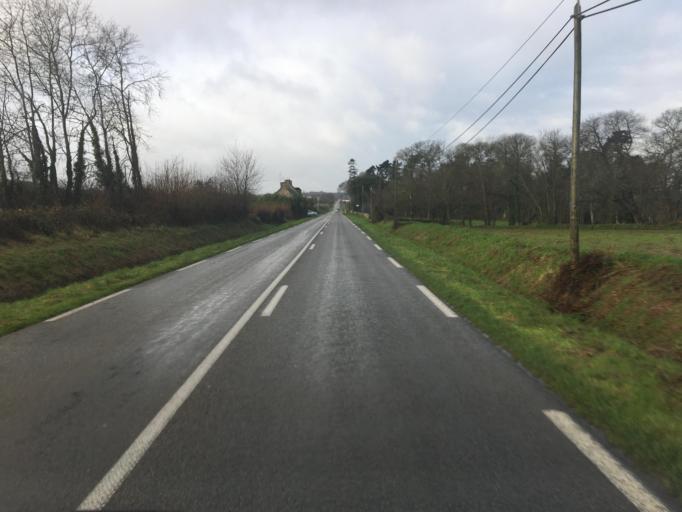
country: FR
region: Lower Normandy
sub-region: Departement de la Manche
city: Saint-Pierre-Eglise
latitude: 49.6683
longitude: -1.3766
